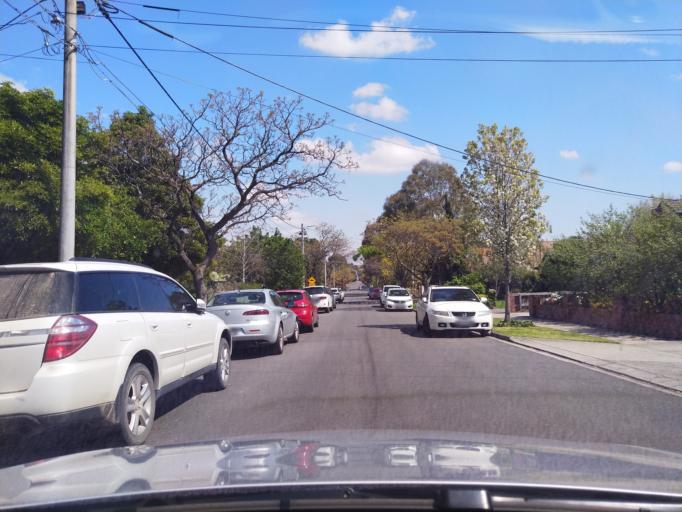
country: AU
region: Victoria
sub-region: Banyule
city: Bellfield
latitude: -37.7596
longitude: 145.0435
